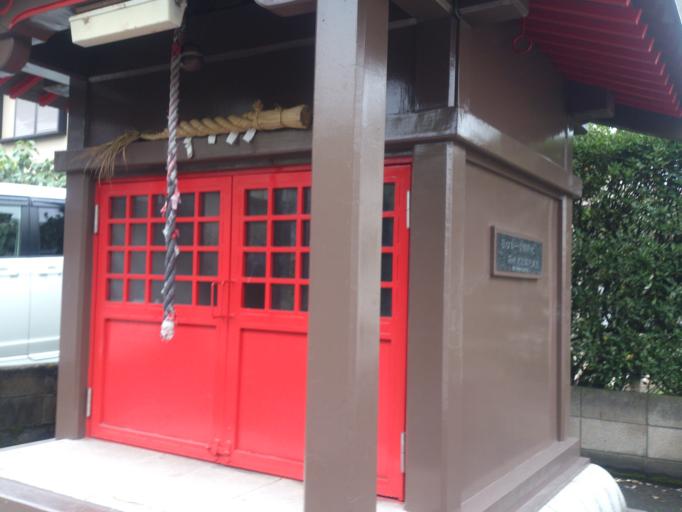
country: JP
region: Chiba
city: Matsudo
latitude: 35.7859
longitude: 139.9179
